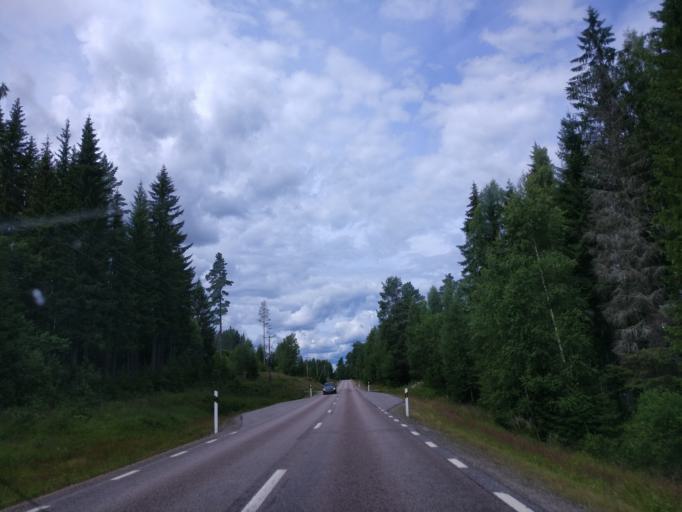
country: SE
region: Vaermland
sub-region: Hagfors Kommun
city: Ekshaerad
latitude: 60.1838
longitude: 13.3441
